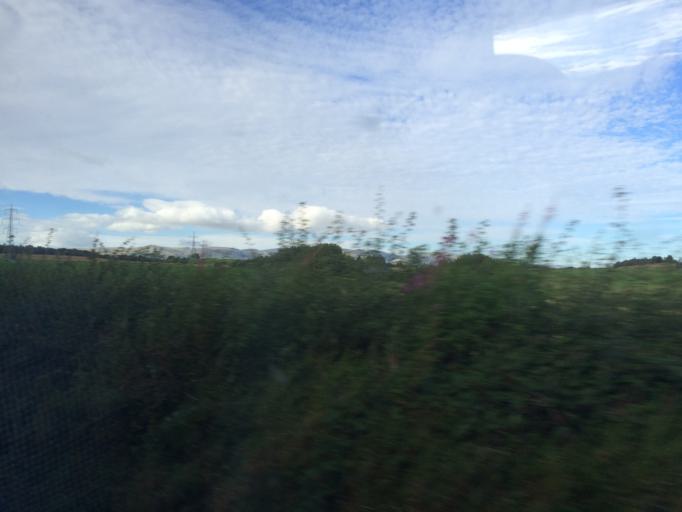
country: GB
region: Scotland
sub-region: Stirling
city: Cowie
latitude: 56.0588
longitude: -3.8508
